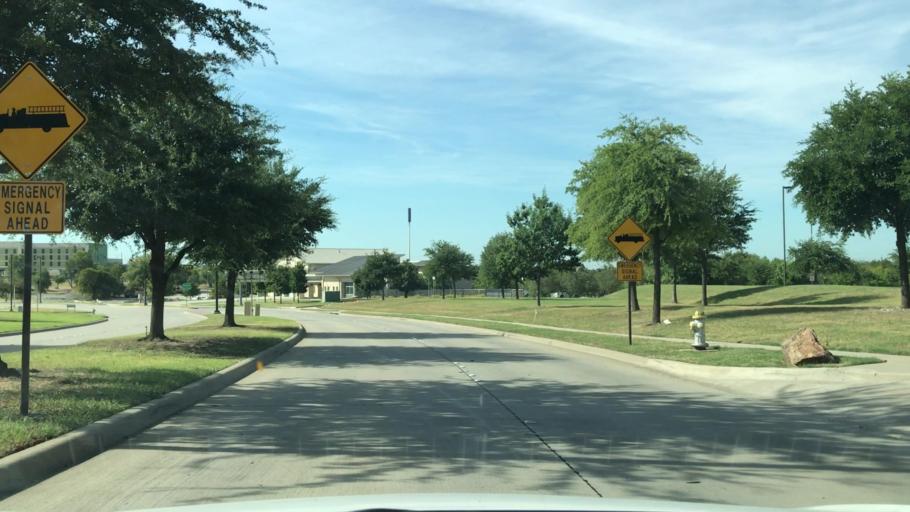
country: US
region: Texas
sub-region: Denton County
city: The Colony
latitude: 33.0740
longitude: -96.8370
